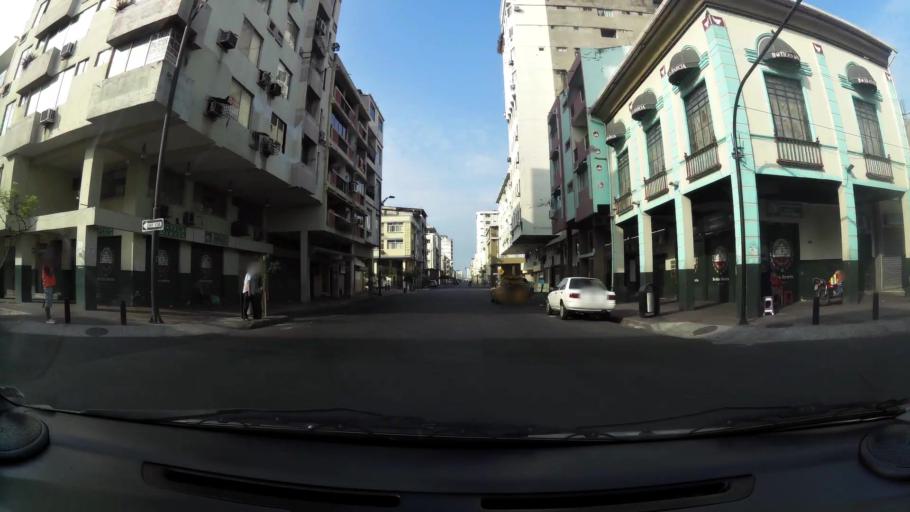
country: EC
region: Guayas
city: Guayaquil
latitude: -2.1967
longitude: -79.8878
